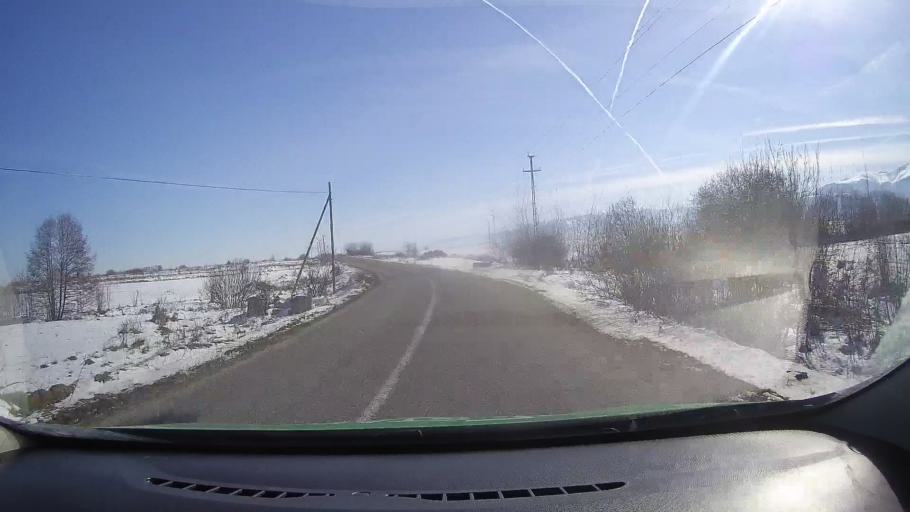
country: RO
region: Brasov
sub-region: Comuna Sambata de Sus
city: Sambata de Sus
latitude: 45.7616
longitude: 24.8050
